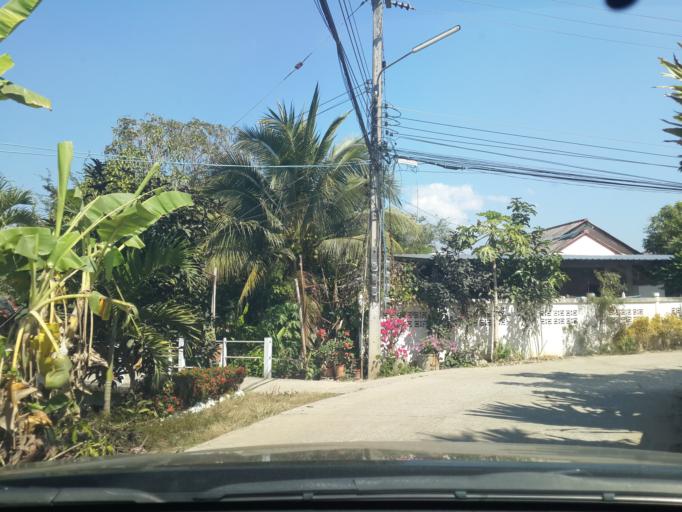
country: TH
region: Chiang Mai
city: San Sai
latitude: 18.8905
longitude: 99.1178
